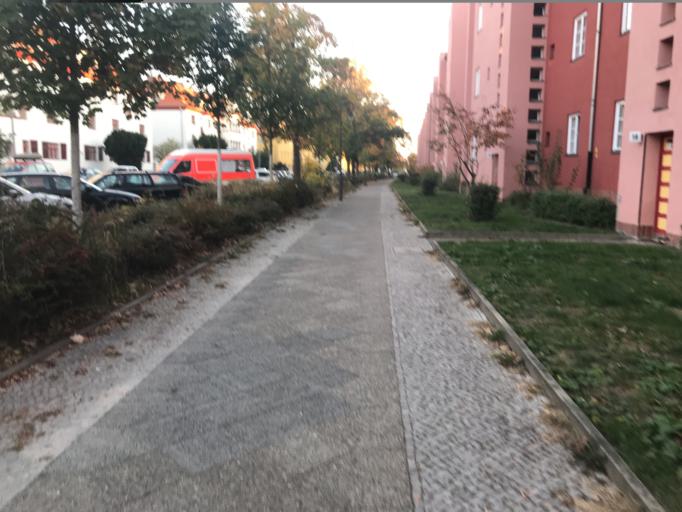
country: DE
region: Berlin
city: Britz
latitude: 52.4508
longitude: 13.4496
